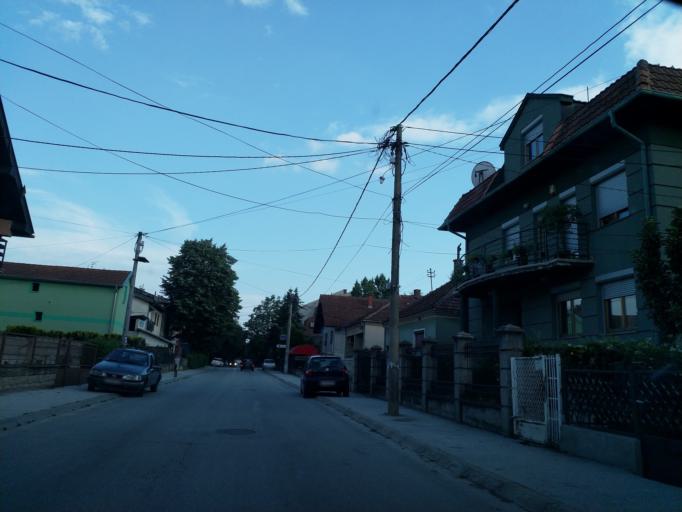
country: RS
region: Central Serbia
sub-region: Pomoravski Okrug
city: Jagodina
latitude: 43.9804
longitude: 21.2457
